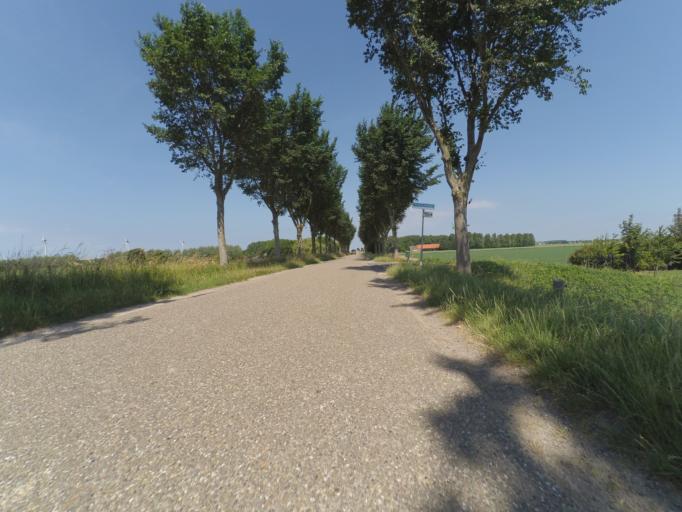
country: NL
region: South Holland
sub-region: Gemeente Goeree-Overflakkee
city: Middelharnis
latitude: 51.6902
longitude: 4.1842
